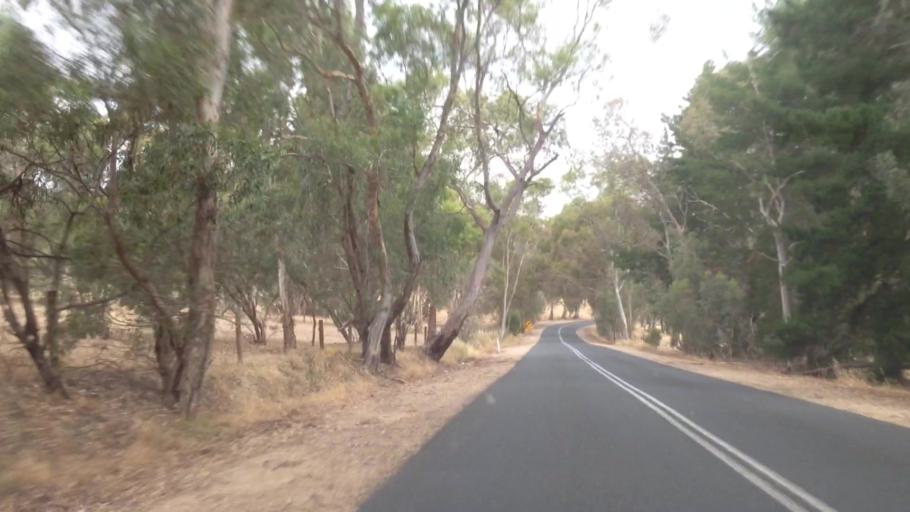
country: AU
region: South Australia
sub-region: Barossa
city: Williamstown
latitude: -34.6485
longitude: 138.8622
